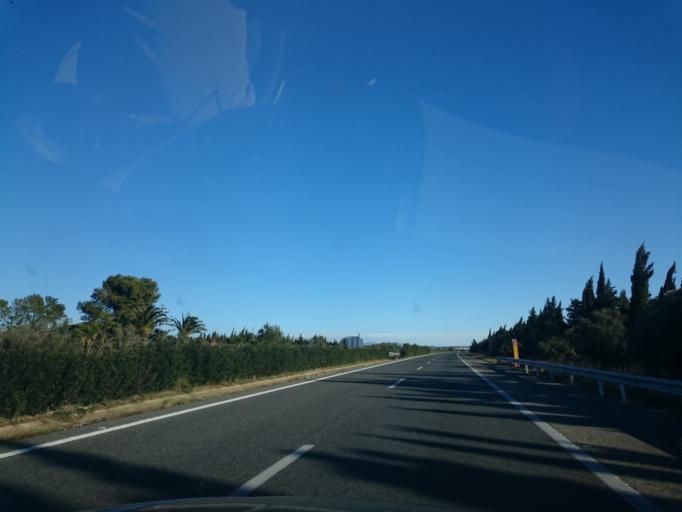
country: ES
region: Catalonia
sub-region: Provincia de Tarragona
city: Camarles
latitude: 40.7770
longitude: 0.6421
